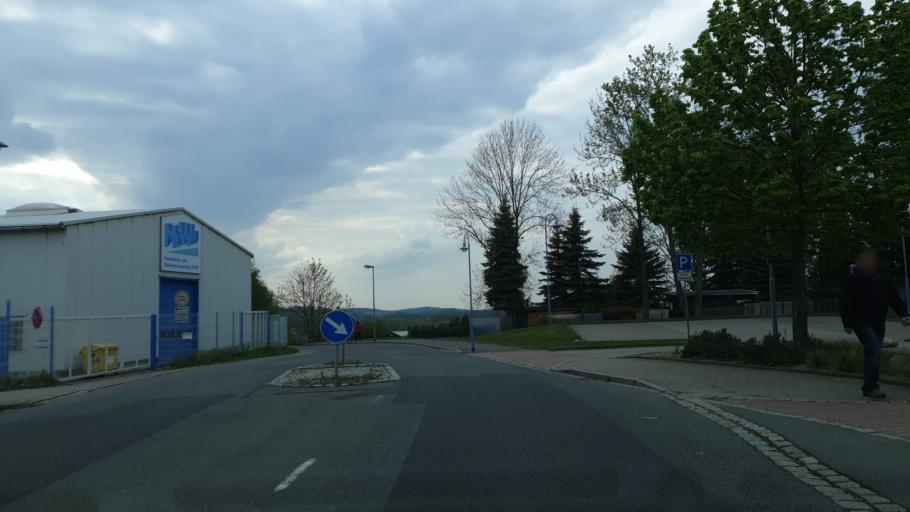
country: DE
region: Saxony
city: Oelsnitz
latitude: 50.7242
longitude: 12.7242
